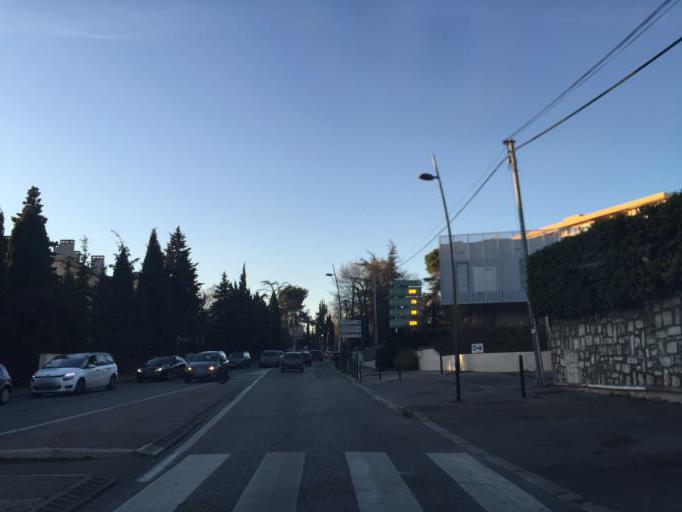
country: FR
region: Provence-Alpes-Cote d'Azur
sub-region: Departement des Bouches-du-Rhone
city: Aix-en-Provence
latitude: 43.5166
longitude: 5.4668
